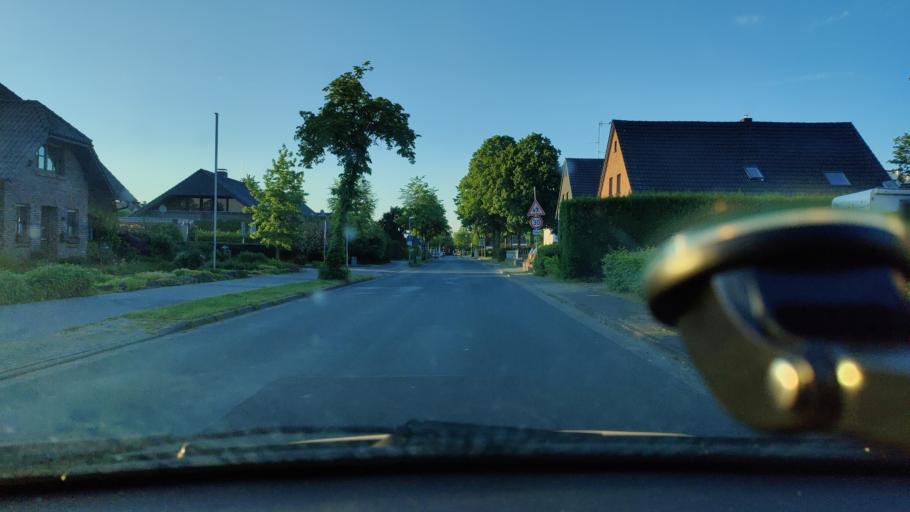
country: DE
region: North Rhine-Westphalia
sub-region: Regierungsbezirk Dusseldorf
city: Kranenburg
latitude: 51.7813
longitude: 6.0150
